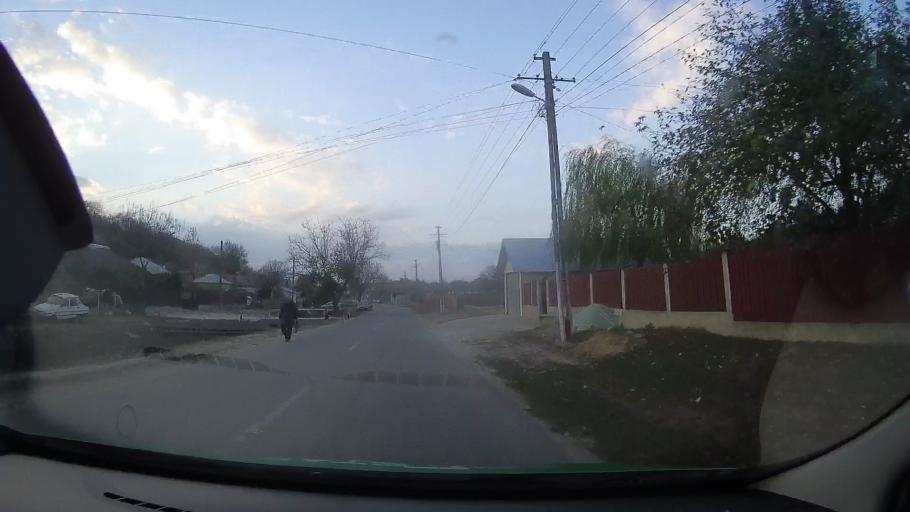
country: RO
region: Constanta
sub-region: Comuna Baneasa
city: Baneasa
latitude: 44.0612
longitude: 27.7064
